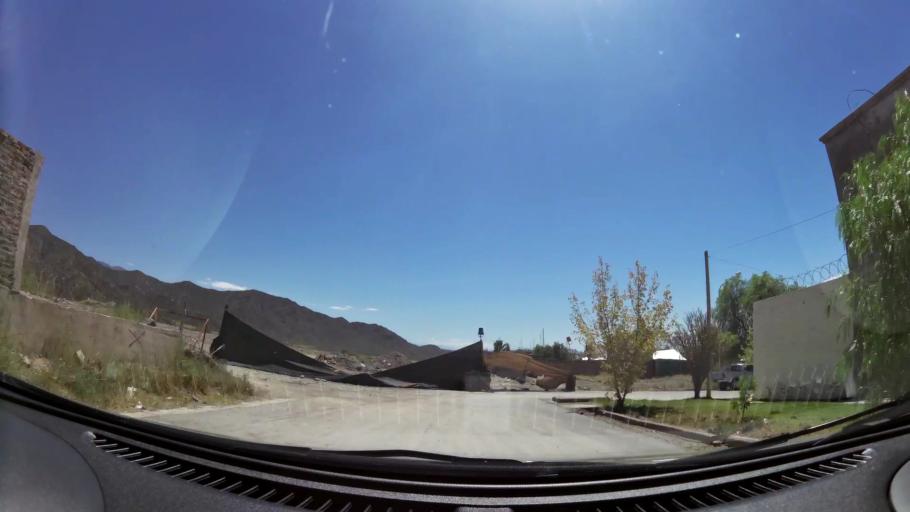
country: AR
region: Mendoza
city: Las Heras
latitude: -32.8450
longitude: -68.8755
